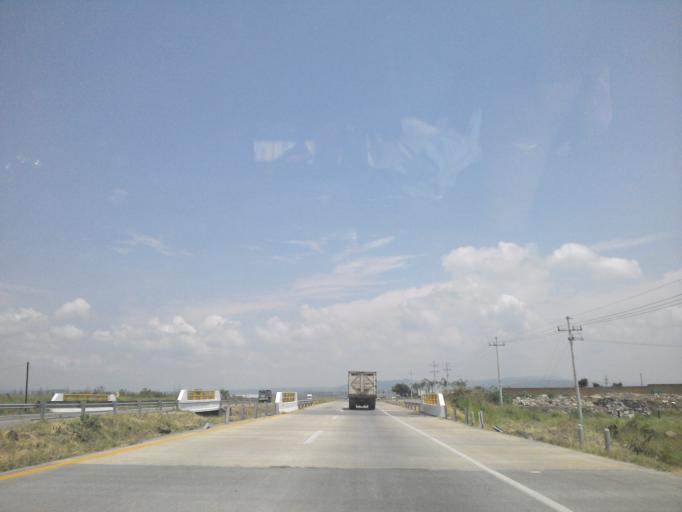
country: MX
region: Jalisco
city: Puente Grande
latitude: 20.5749
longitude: -103.1612
